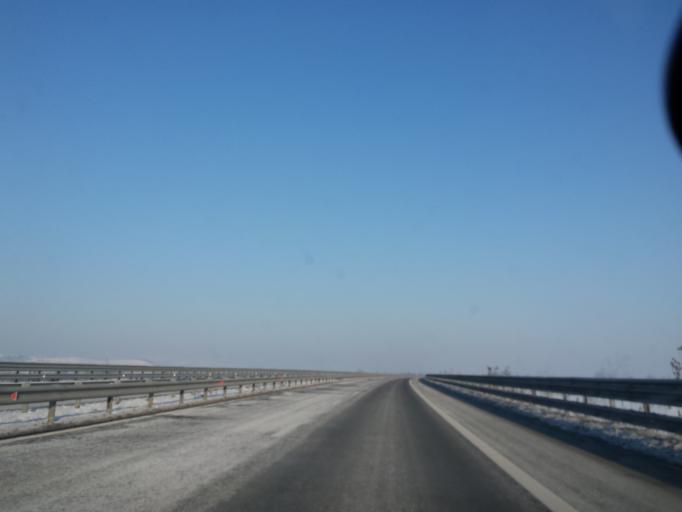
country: RO
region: Hunedoara
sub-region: Comuna Turdas
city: Pricaz
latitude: 45.8702
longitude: 23.1622
